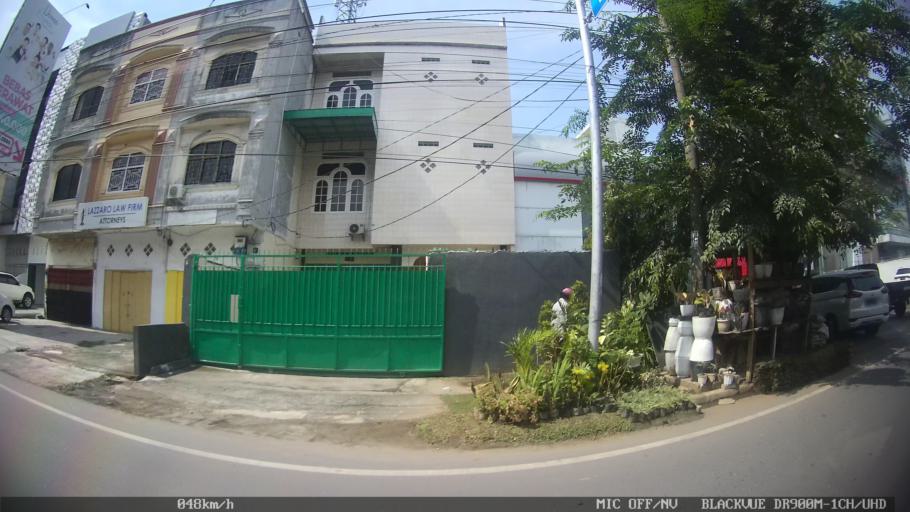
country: ID
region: North Sumatra
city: Medan
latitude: 3.6071
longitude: 98.6678
